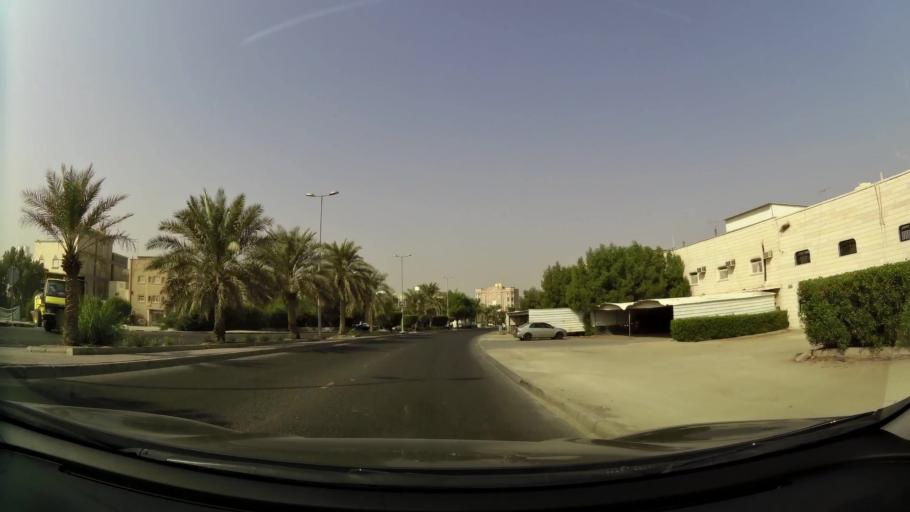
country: KW
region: Al Asimah
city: Ar Rabiyah
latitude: 29.2801
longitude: 47.8815
